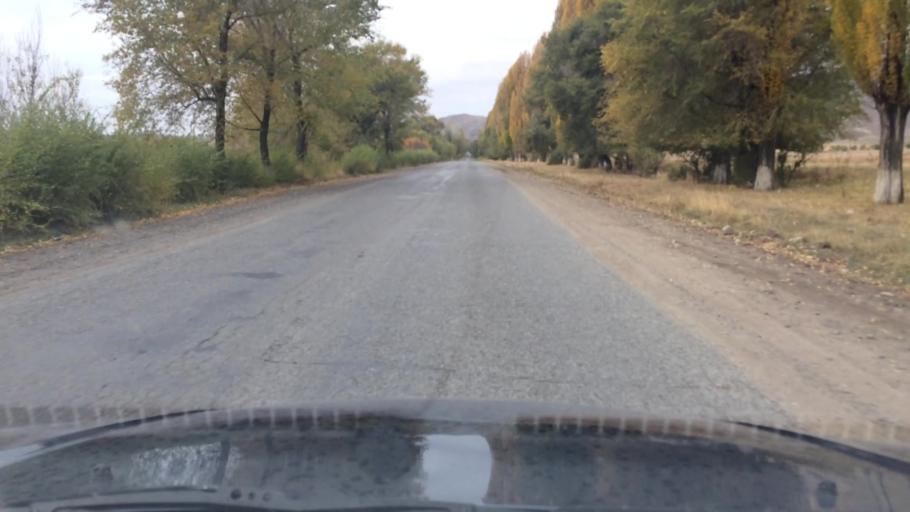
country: KG
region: Ysyk-Koel
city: Pokrovka
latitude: 42.7376
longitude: 77.9262
